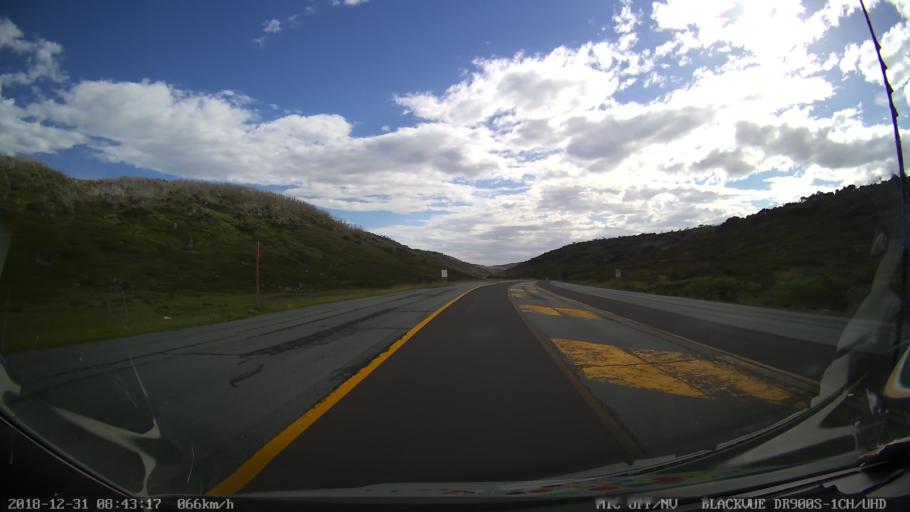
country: AU
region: New South Wales
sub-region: Snowy River
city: Jindabyne
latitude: -36.3901
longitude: 148.4426
